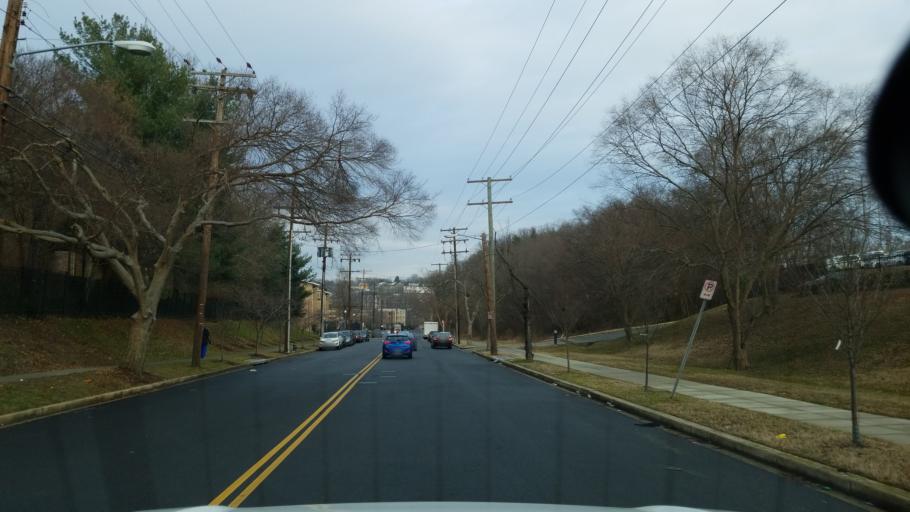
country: US
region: Maryland
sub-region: Prince George's County
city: Glassmanor
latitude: 38.8349
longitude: -76.9859
